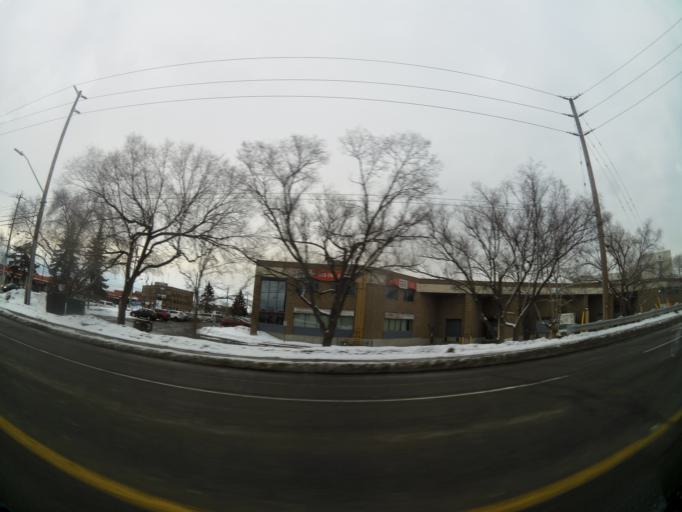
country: CA
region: Quebec
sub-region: Outaouais
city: Gatineau
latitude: 45.4519
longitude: -75.5892
